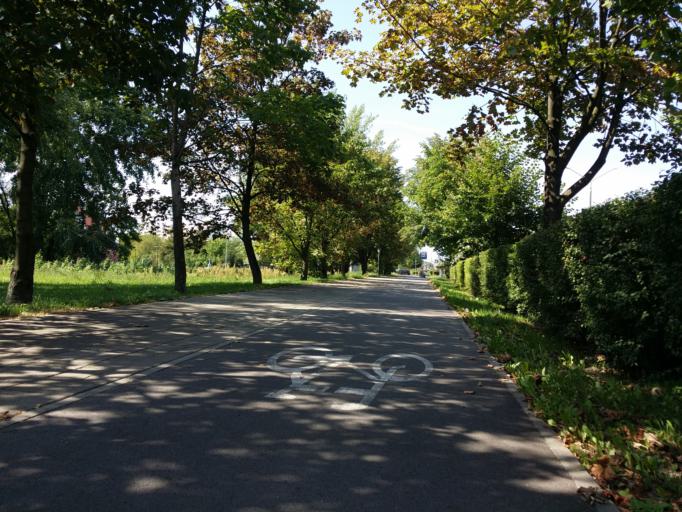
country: PL
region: Masovian Voivodeship
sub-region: Radom
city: Radom
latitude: 51.3828
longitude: 21.1638
